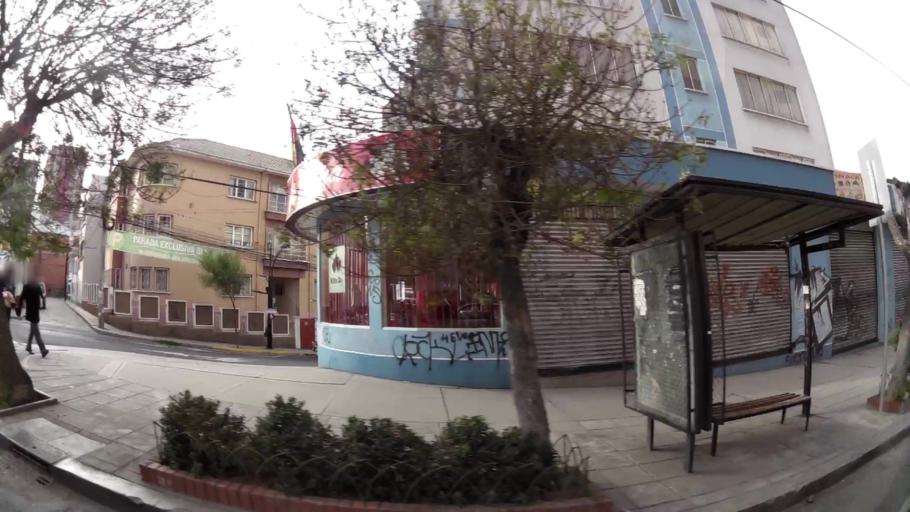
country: BO
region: La Paz
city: La Paz
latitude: -16.4960
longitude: -68.1233
